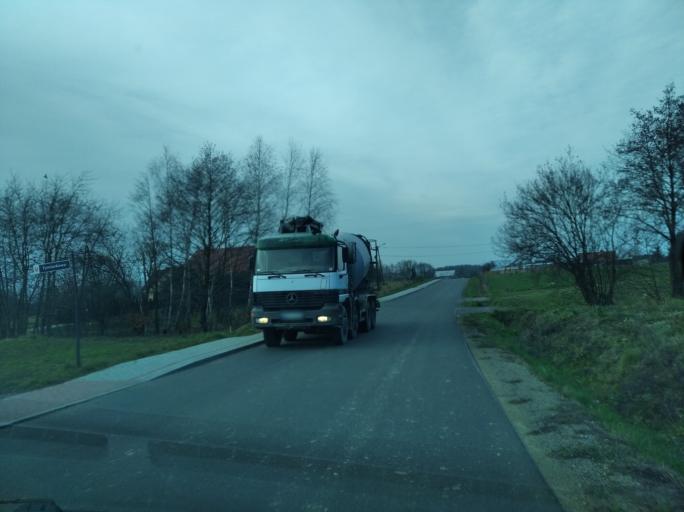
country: PL
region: Subcarpathian Voivodeship
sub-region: Powiat ropczycko-sedziszowski
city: Sedziszow Malopolski
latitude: 50.0855
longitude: 21.7110
